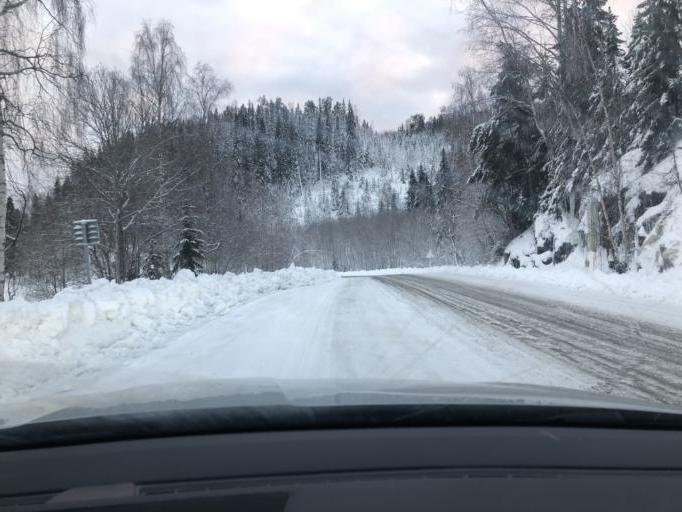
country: SE
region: Vaesternorrland
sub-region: Kramfors Kommun
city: Nordingra
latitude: 62.9516
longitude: 18.2462
